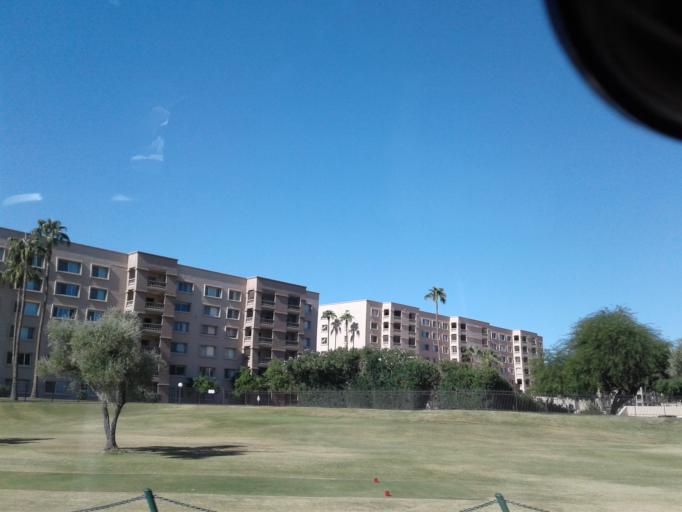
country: US
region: Arizona
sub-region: Maricopa County
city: Scottsdale
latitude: 33.5038
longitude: -111.9089
